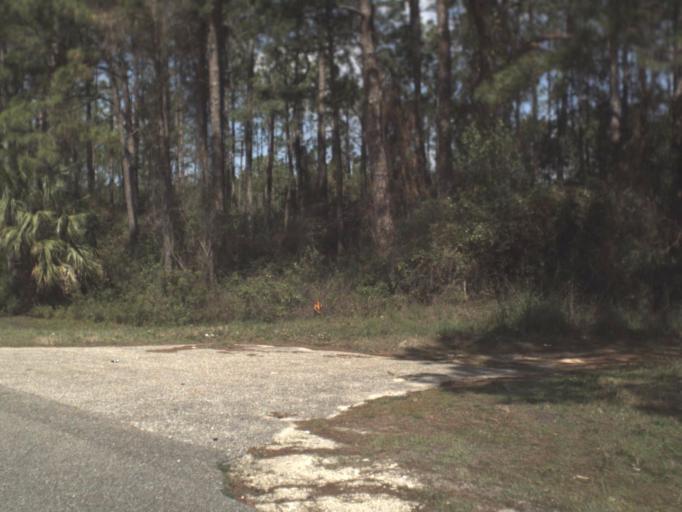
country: US
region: Florida
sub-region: Franklin County
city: Apalachicola
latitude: 29.7340
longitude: -85.1500
